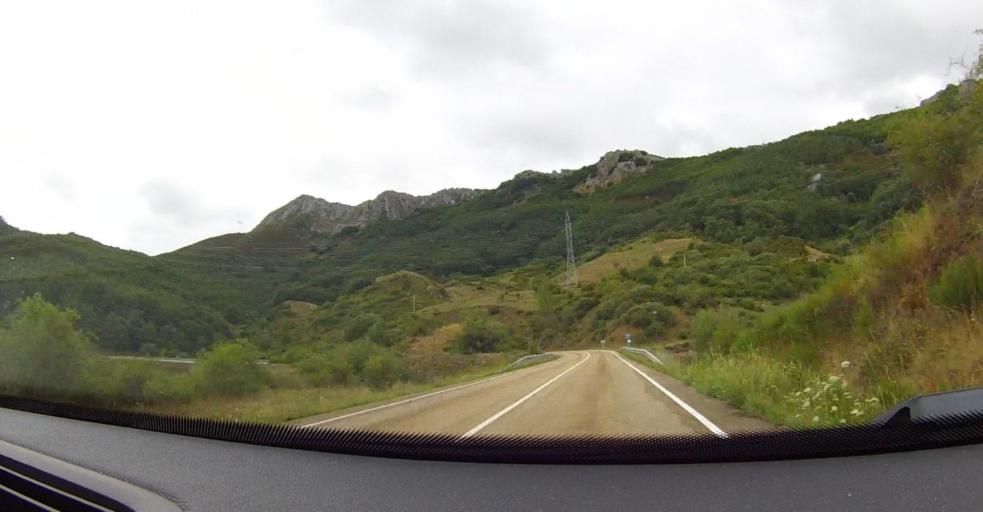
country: ES
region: Castille and Leon
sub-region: Provincia de Leon
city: Puebla de Lillo
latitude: 42.9341
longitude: -5.2746
